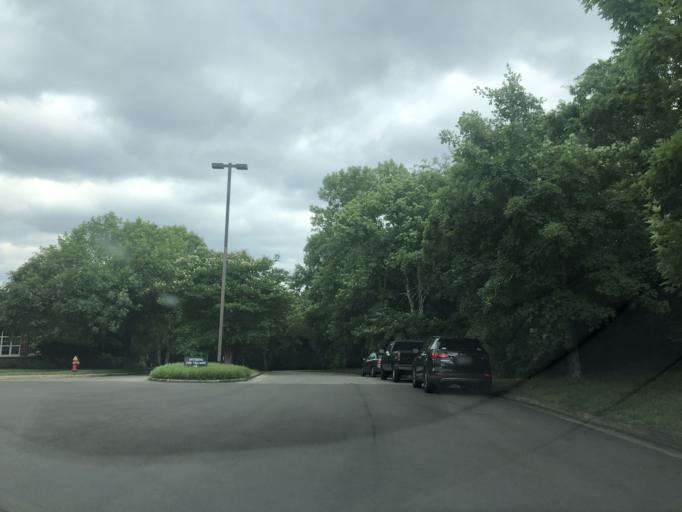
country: US
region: Tennessee
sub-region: Davidson County
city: Forest Hills
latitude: 36.0929
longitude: -86.8219
